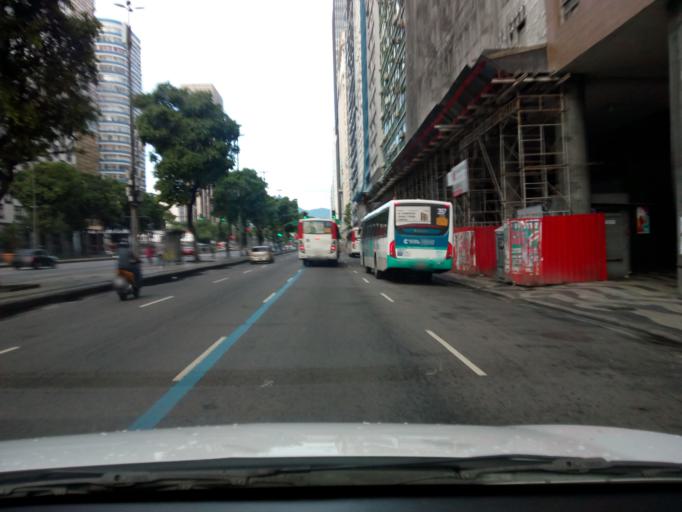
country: BR
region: Rio de Janeiro
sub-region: Rio De Janeiro
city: Rio de Janeiro
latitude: -22.9013
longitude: -43.1796
